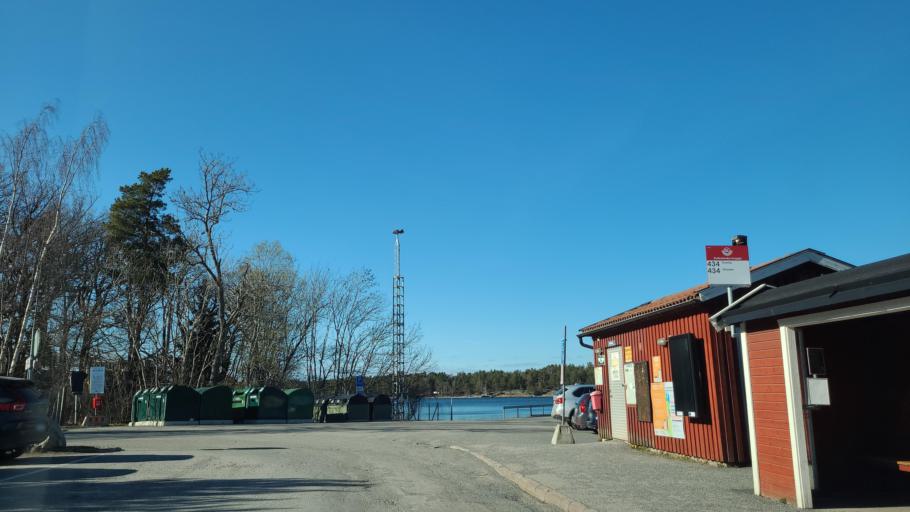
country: SE
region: Stockholm
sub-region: Varmdo Kommun
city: Holo
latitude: 59.3724
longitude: 18.6985
